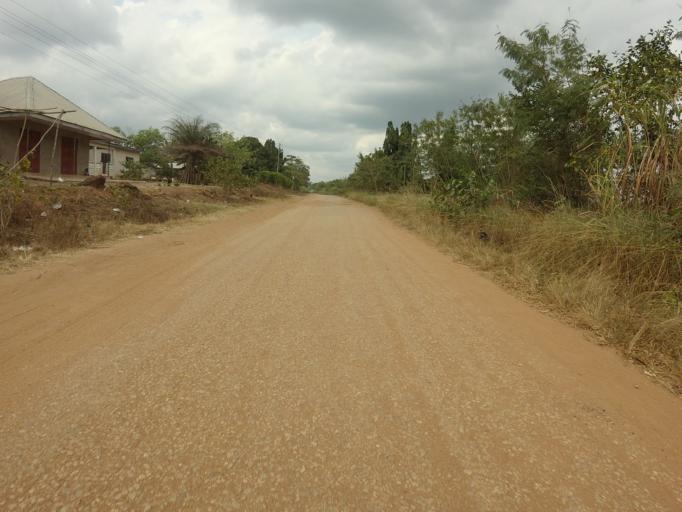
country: GH
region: Volta
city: Ho
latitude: 6.6550
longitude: 0.3443
